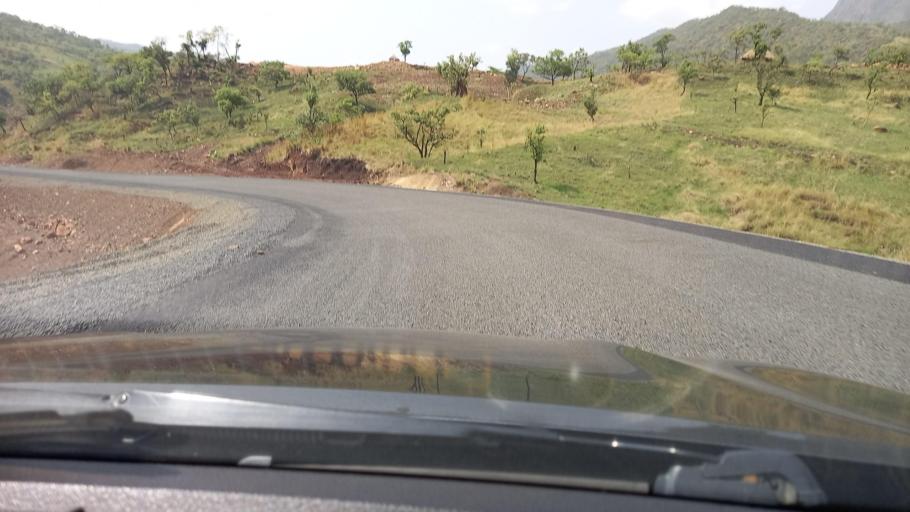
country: ET
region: Southern Nations, Nationalities, and People's Region
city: Mizan Teferi
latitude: 6.1943
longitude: 35.6728
